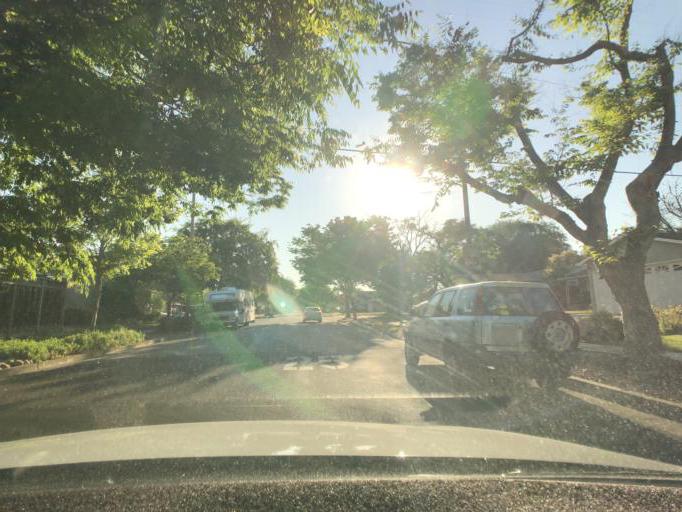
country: US
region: California
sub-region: Santa Clara County
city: Cambrian Park
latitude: 37.2427
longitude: -121.9250
